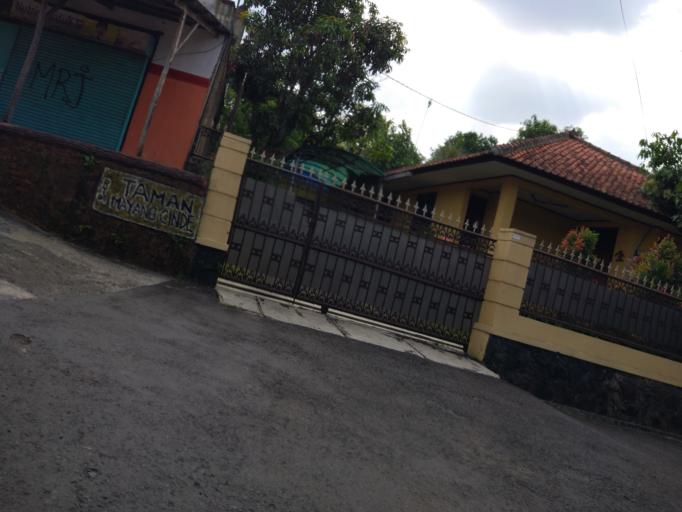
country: ID
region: West Java
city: Bandung
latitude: -6.9040
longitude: 107.6890
